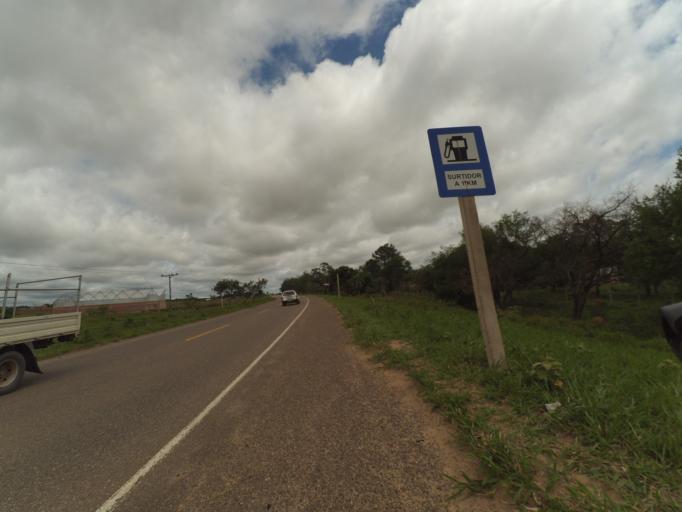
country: BO
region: Santa Cruz
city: Santa Rita
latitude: -17.9065
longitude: -63.2521
